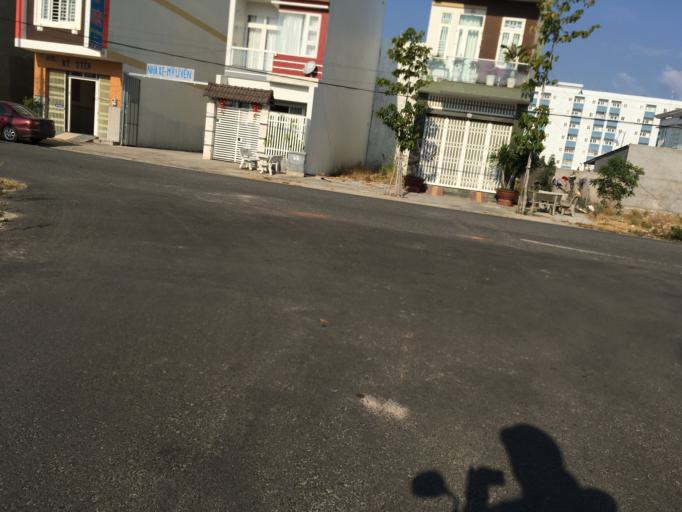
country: VN
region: Ninh Thuan
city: Phan Rang-Thap Cham
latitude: 11.5642
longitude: 109.0180
